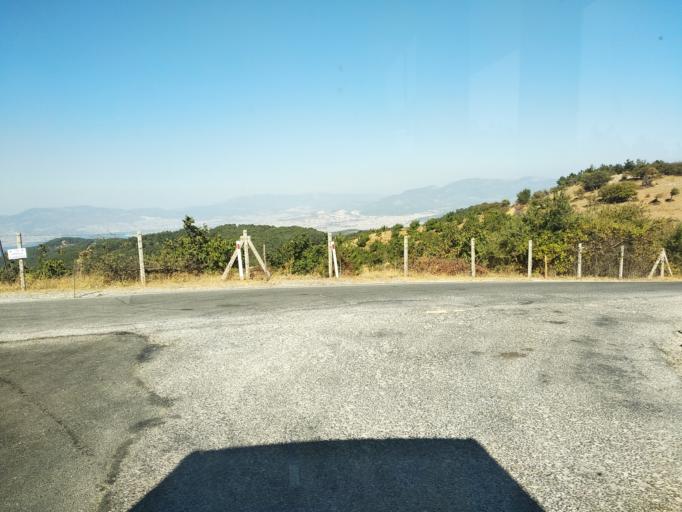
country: TR
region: Izmir
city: Gaziemir
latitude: 38.3190
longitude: 27.0122
